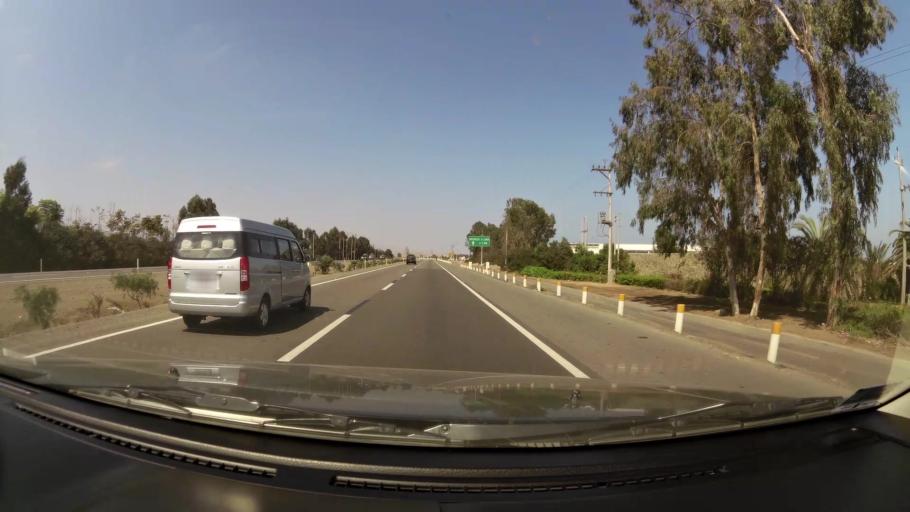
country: PE
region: Lima
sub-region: Provincia de Canete
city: Asia
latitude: -12.7748
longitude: -76.5890
